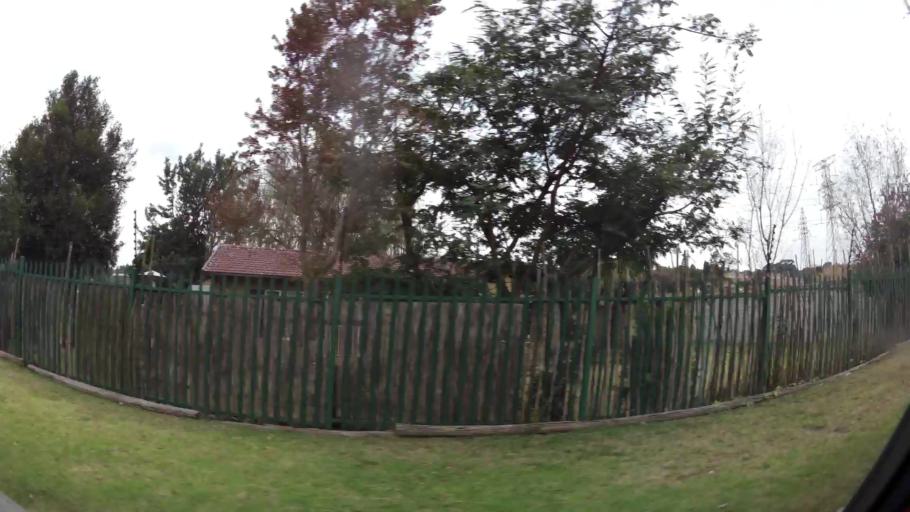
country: ZA
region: Gauteng
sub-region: City of Johannesburg Metropolitan Municipality
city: Roodepoort
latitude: -26.1203
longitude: 27.9087
